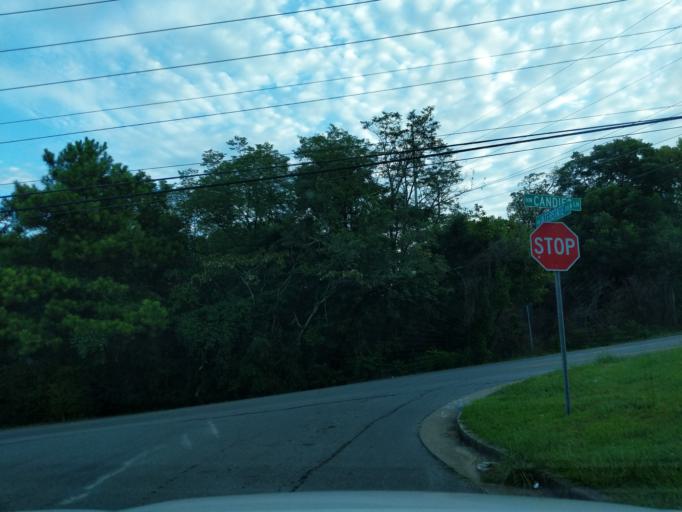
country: US
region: Tennessee
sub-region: Bradley County
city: Cleveland
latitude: 35.1952
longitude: -84.8897
